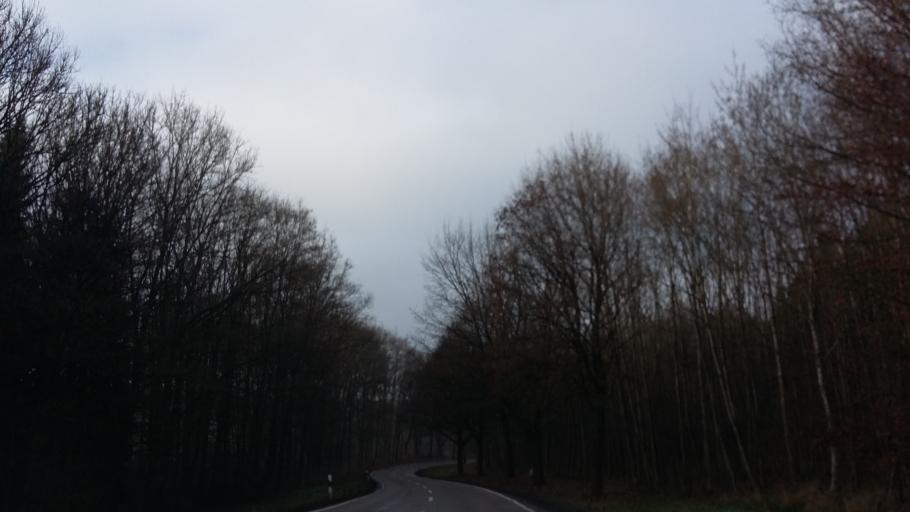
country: DE
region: Bavaria
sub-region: Swabia
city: Sielenbach
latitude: 48.4193
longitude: 11.1569
